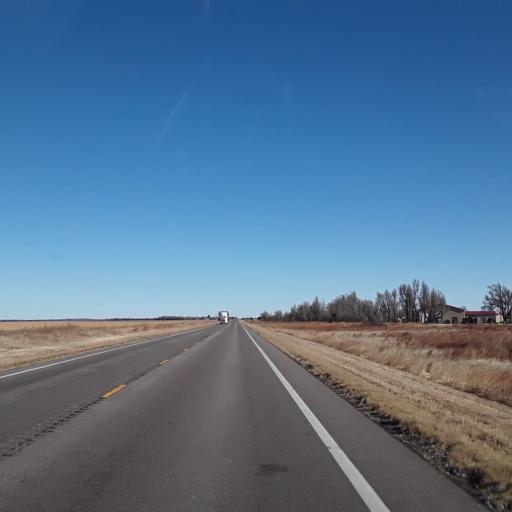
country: US
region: Kansas
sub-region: Pawnee County
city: Larned
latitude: 38.0949
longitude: -99.2154
